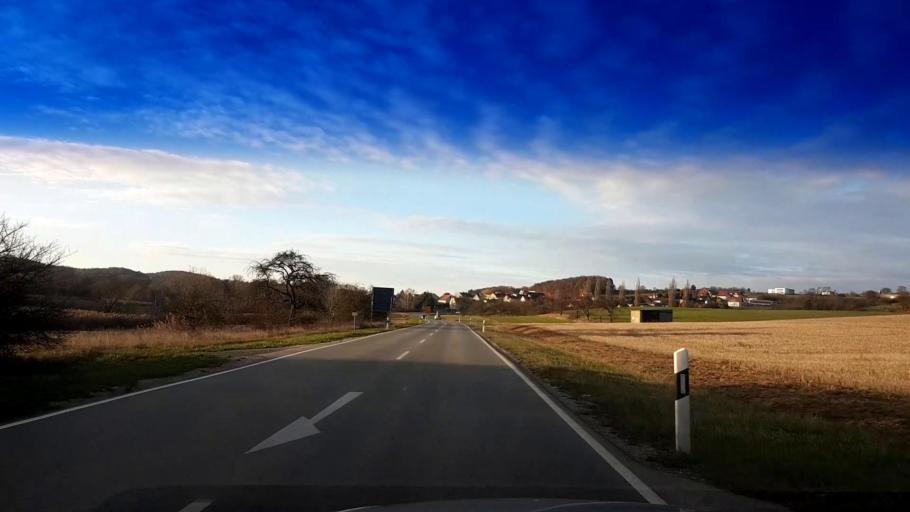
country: DE
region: Bavaria
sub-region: Upper Franconia
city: Priesendorf
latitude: 49.8914
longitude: 10.7364
